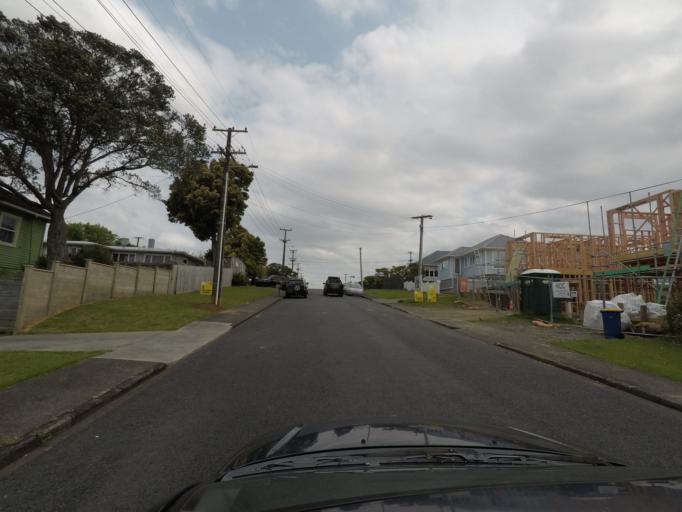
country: NZ
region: Auckland
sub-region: Auckland
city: Rosebank
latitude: -36.8262
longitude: 174.6464
